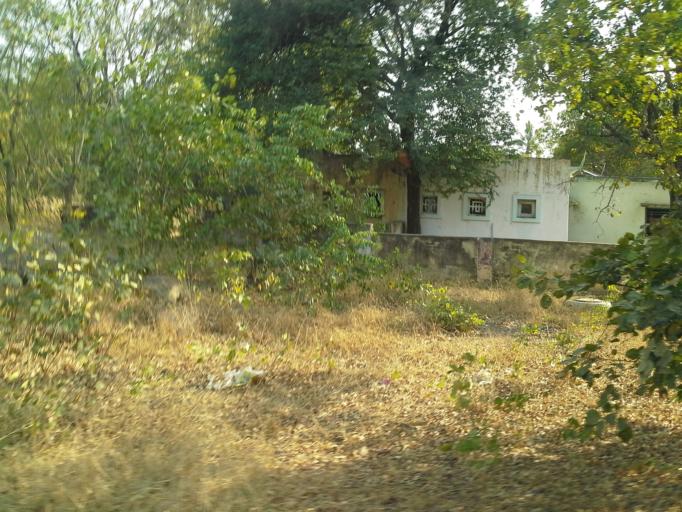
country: IN
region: Telangana
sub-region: Hyderabad
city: Hyderabad
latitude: 17.3145
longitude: 78.4153
